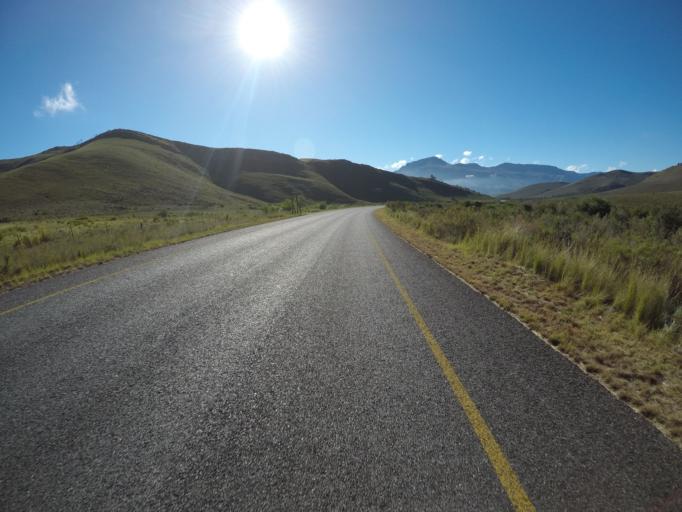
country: ZA
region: Western Cape
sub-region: Overberg District Municipality
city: Caledon
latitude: -34.0840
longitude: 19.5523
